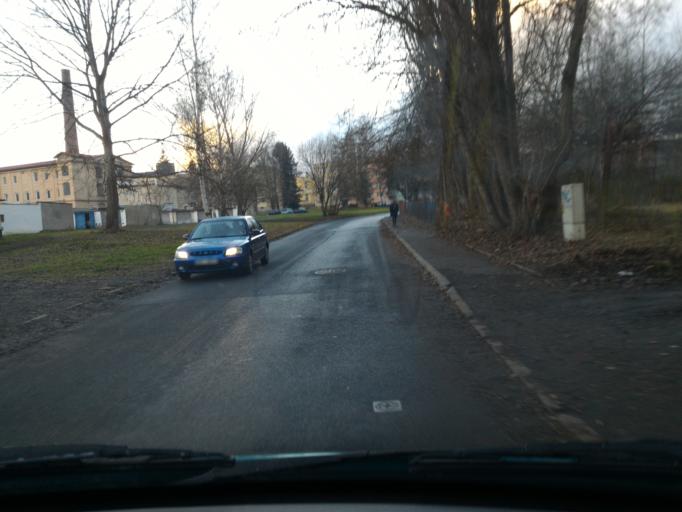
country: CZ
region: Ustecky
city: Varnsdorf
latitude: 50.9038
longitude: 14.6272
